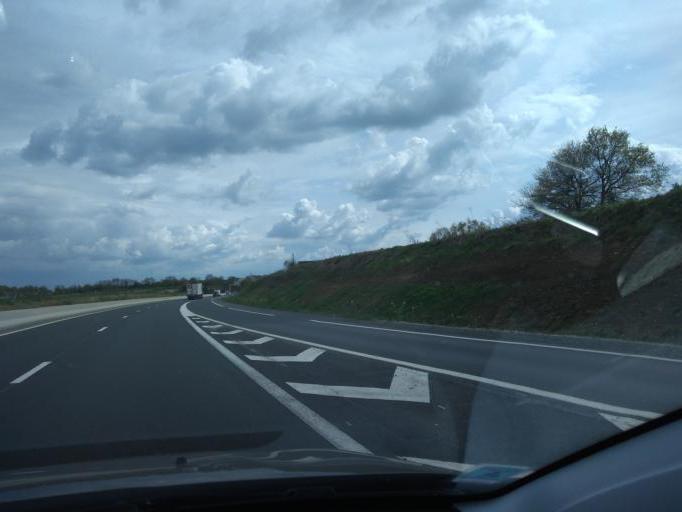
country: FR
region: Pays de la Loire
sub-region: Departement de Maine-et-Loire
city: Grez-Neuville
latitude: 47.5804
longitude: -0.6866
